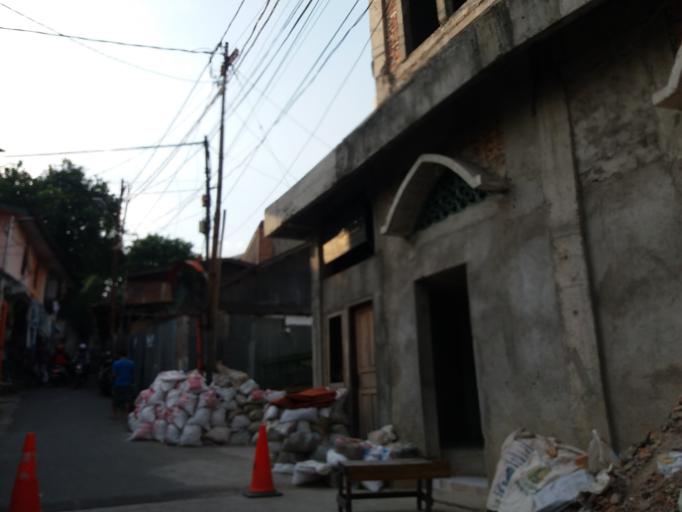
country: ID
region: Jakarta Raya
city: Jakarta
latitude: -6.2449
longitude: 106.8111
